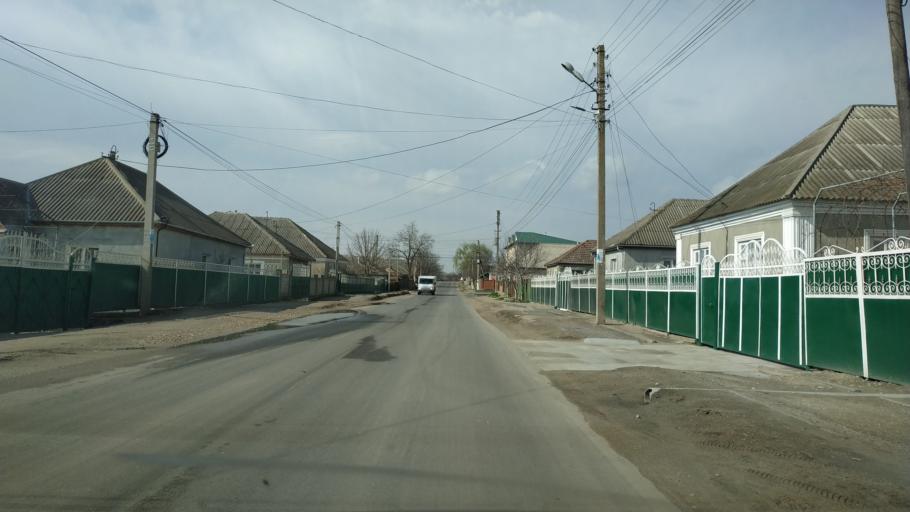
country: MD
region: Gagauzia
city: Vulcanesti
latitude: 45.6760
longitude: 28.4159
